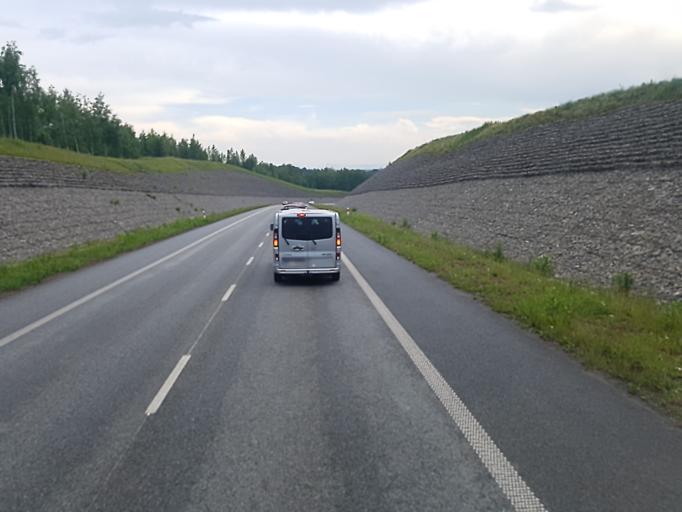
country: PL
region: Silesian Voivodeship
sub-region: Jastrzebie-Zdroj
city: Jastrzebie Zdroj
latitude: 49.9676
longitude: 18.5574
